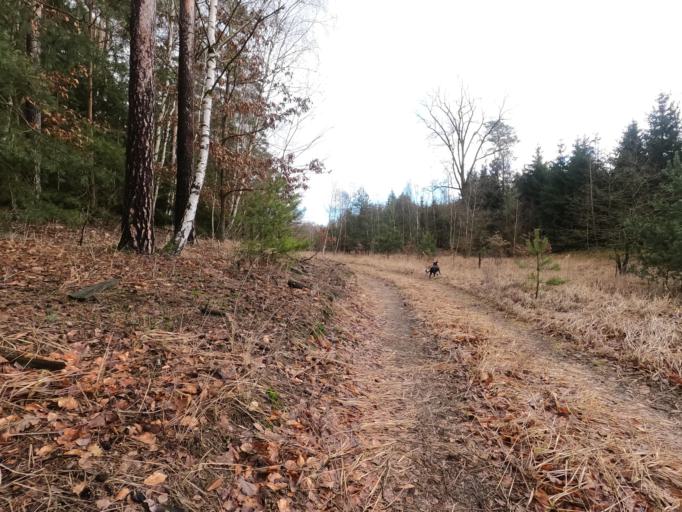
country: PL
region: Greater Poland Voivodeship
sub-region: Powiat pilski
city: Miasteczko Krajenskie
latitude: 53.1157
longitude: 16.9711
